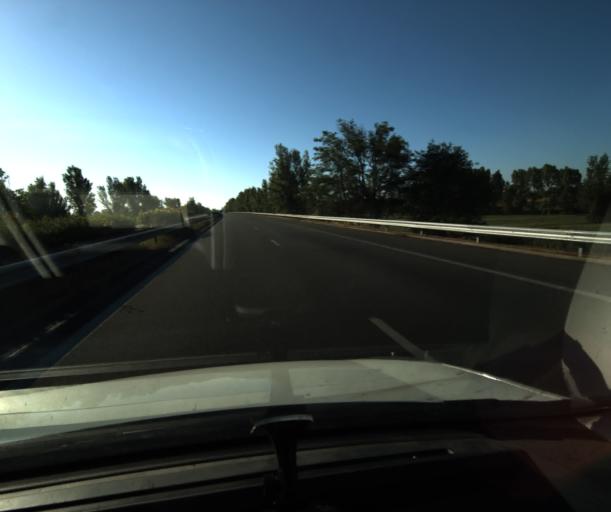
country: FR
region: Midi-Pyrenees
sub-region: Departement du Tarn-et-Garonne
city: Montech
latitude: 43.9855
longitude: 1.2436
